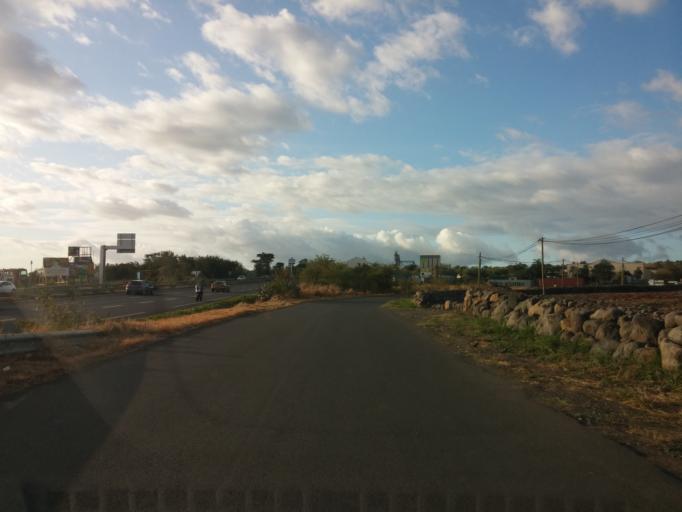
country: RE
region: Reunion
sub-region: Reunion
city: Le Port
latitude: -20.9695
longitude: 55.2991
